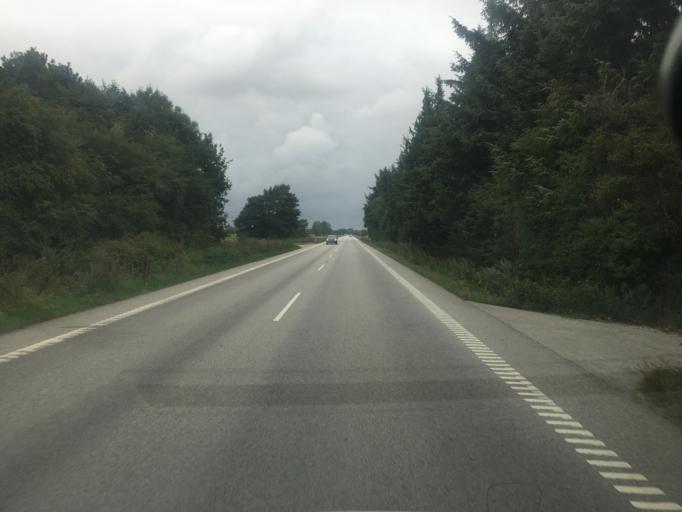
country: DK
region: South Denmark
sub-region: Haderslev Kommune
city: Vojens
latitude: 55.2259
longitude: 9.2999
